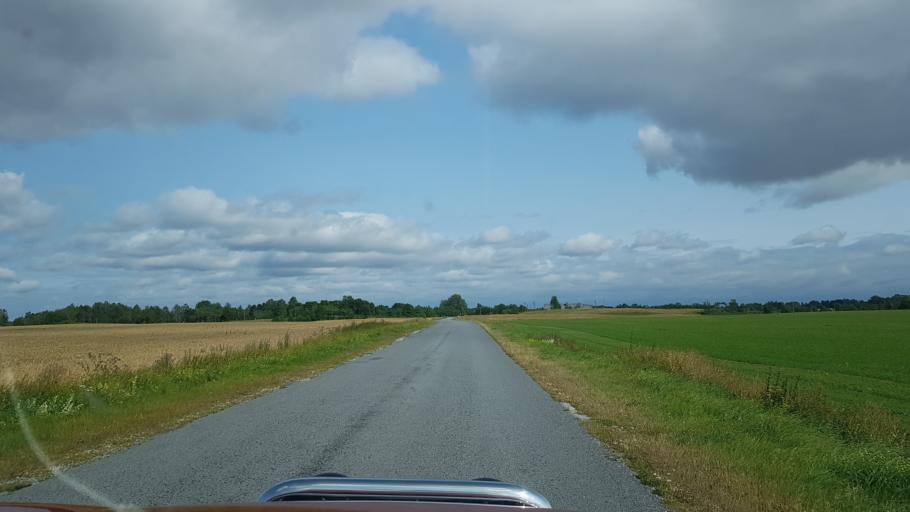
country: EE
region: Laeaene-Virumaa
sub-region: Kadrina vald
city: Kadrina
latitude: 59.3400
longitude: 26.0744
